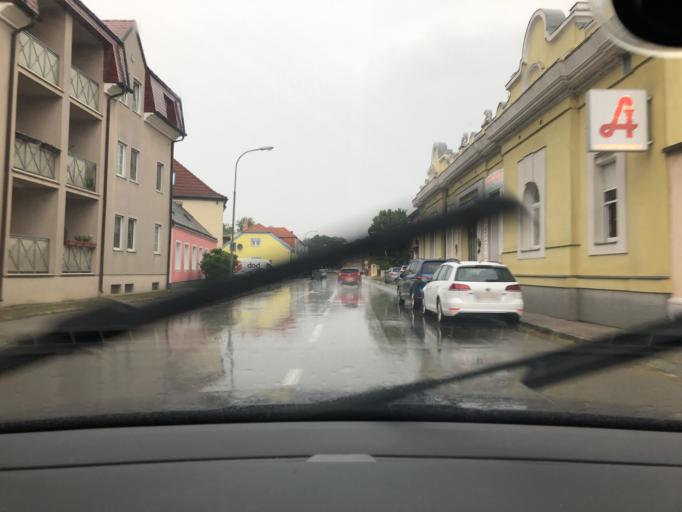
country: AT
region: Lower Austria
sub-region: Politischer Bezirk Ganserndorf
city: Marchegg
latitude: 48.2784
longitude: 16.9106
